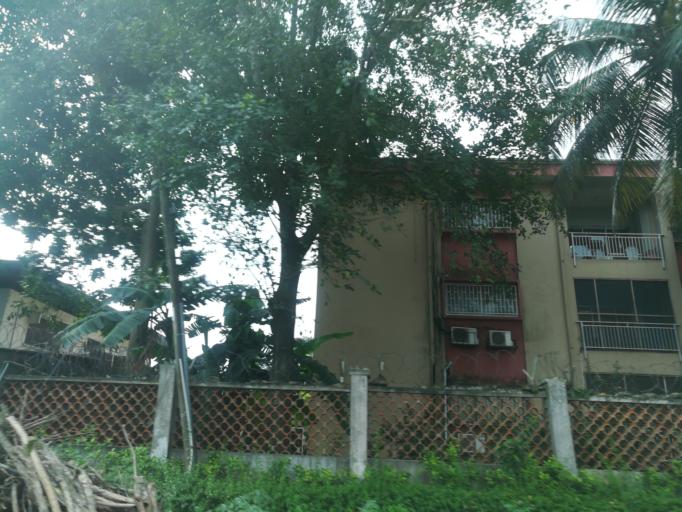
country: NG
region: Lagos
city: Oshodi
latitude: 6.5726
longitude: 3.3557
